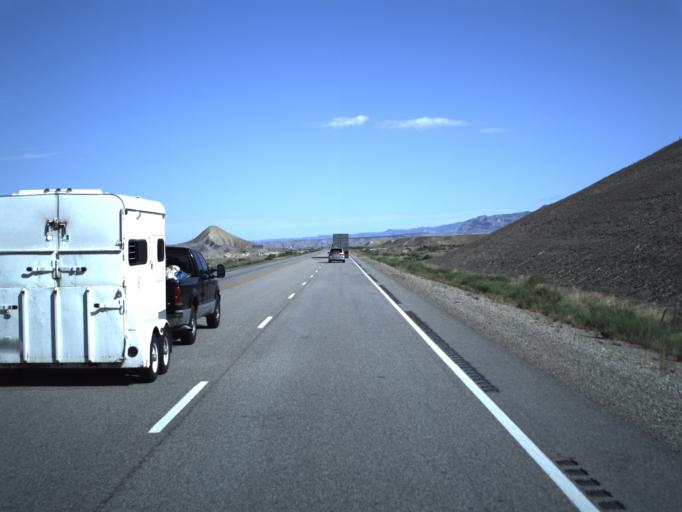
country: US
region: Utah
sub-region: Carbon County
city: East Carbon City
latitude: 39.2850
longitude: -110.3506
